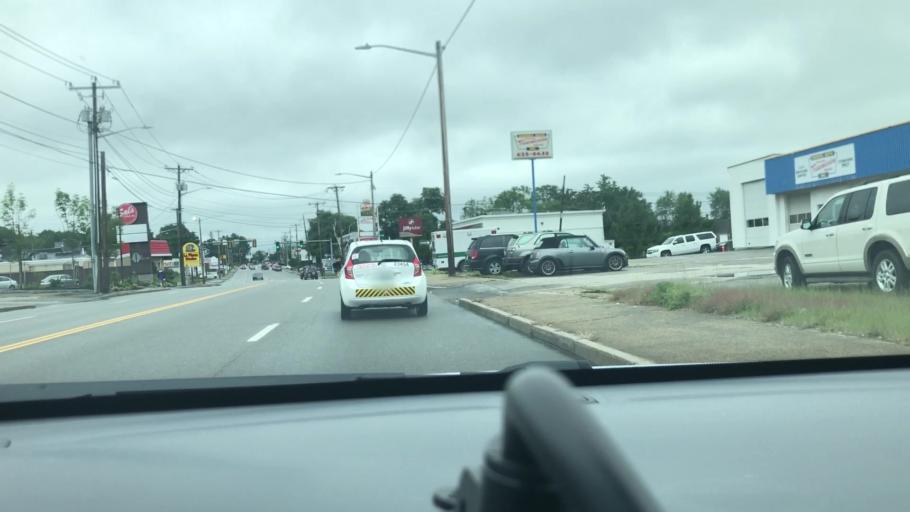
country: US
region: New Hampshire
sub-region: Hillsborough County
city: Manchester
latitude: 42.9703
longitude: -71.4543
